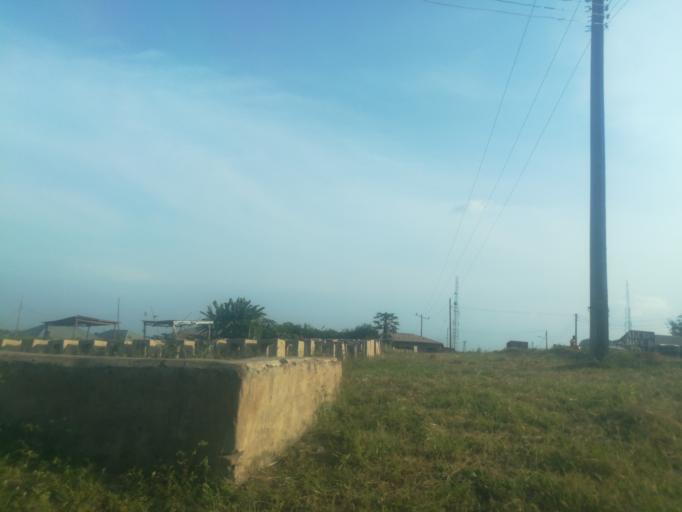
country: NG
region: Oyo
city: Moniya
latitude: 7.5692
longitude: 3.8857
